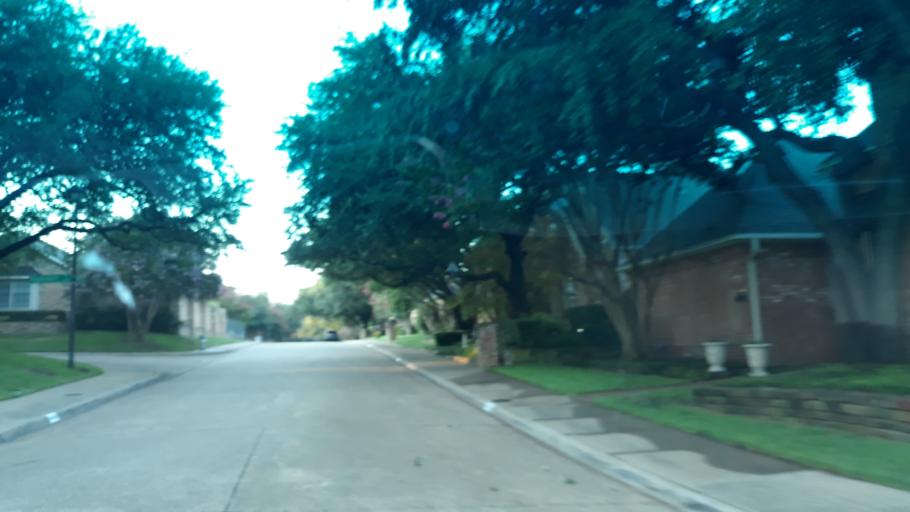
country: US
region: Texas
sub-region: Dallas County
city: Addison
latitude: 32.9404
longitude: -96.8019
